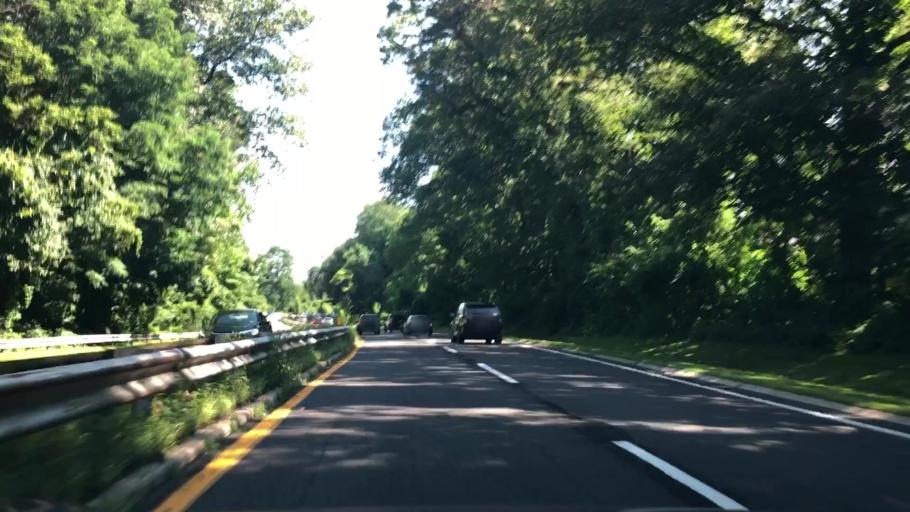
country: US
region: New York
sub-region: Westchester County
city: Hartsdale
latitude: 41.0056
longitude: -73.7990
